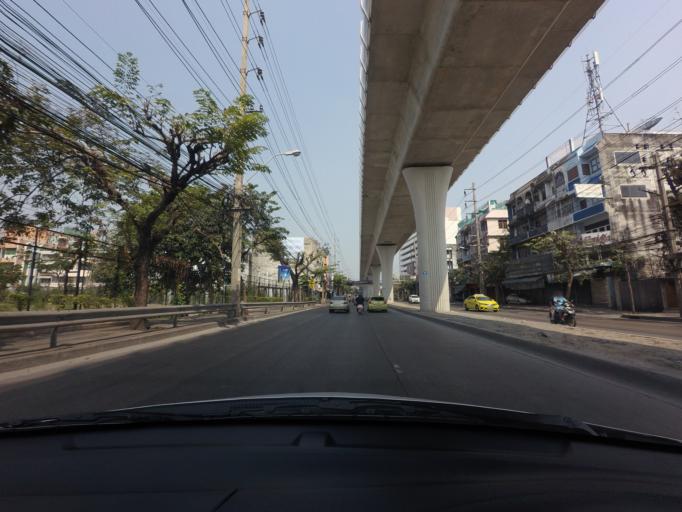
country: TH
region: Bangkok
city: Bangkok Yai
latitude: 13.7362
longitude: 100.4710
